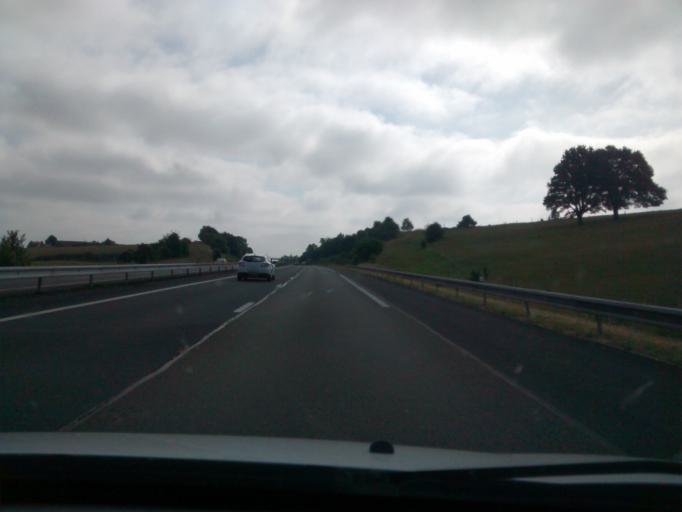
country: FR
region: Pays de la Loire
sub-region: Departement de la Sarthe
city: Coulans-sur-Gee
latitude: 48.0248
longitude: -0.0195
